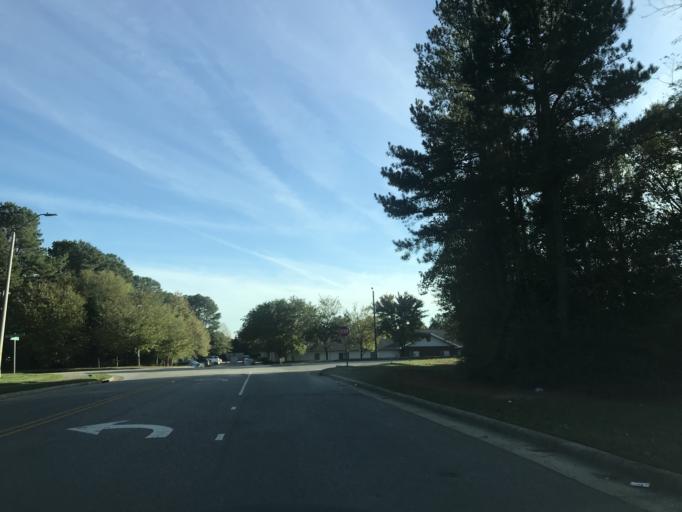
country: US
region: North Carolina
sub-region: Wake County
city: Wake Forest
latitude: 35.8918
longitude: -78.5549
